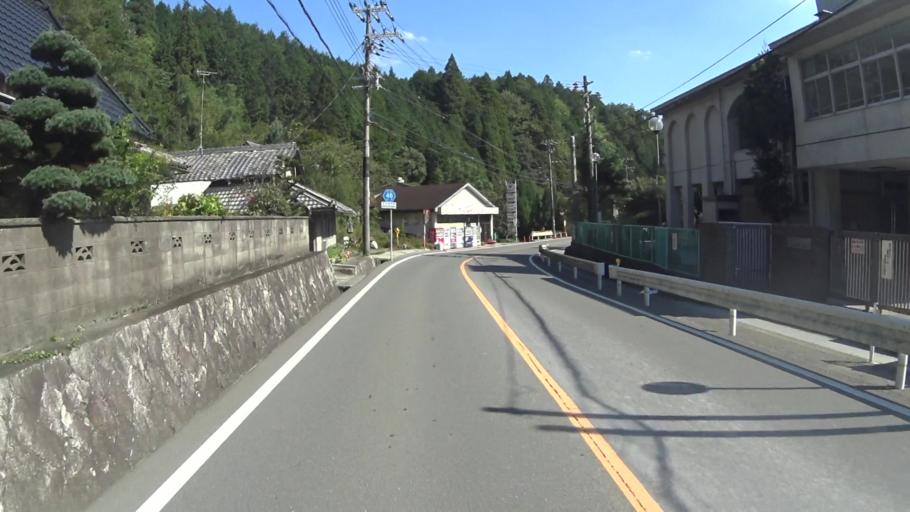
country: JP
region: Kyoto
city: Kameoka
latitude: 34.9453
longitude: 135.5513
